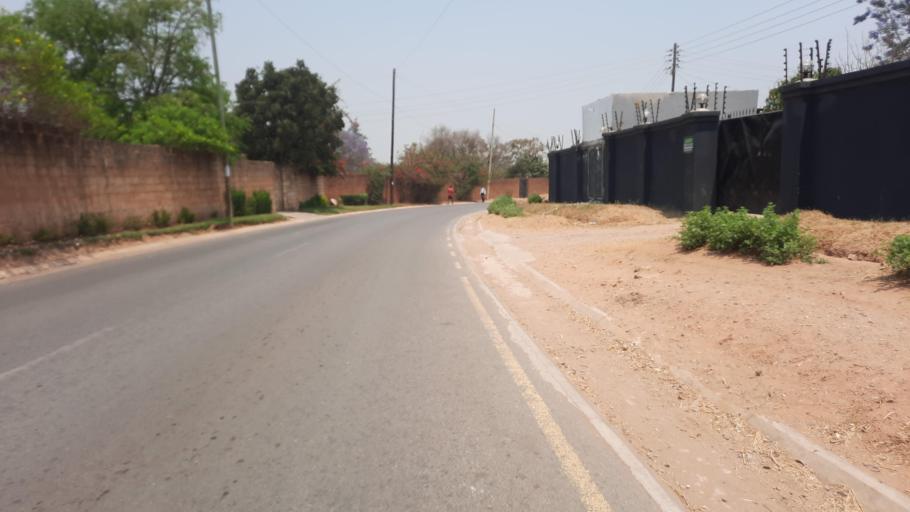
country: ZM
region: Lusaka
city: Lusaka
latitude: -15.4118
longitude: 28.3646
